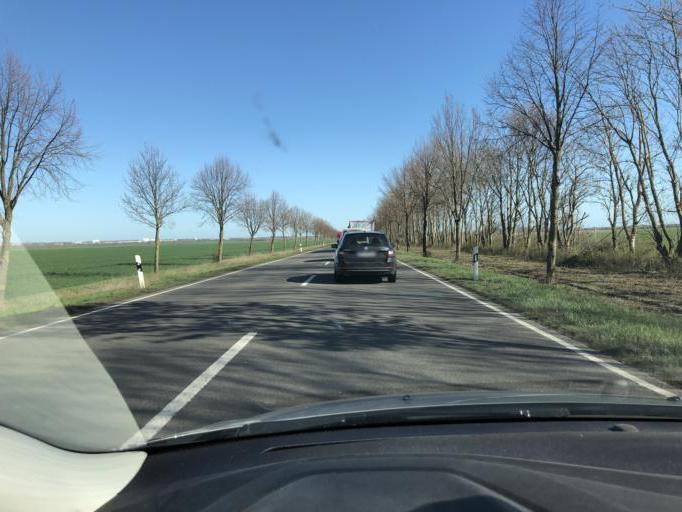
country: DE
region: Saxony-Anhalt
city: Welsleben
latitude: 52.0134
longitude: 11.6068
